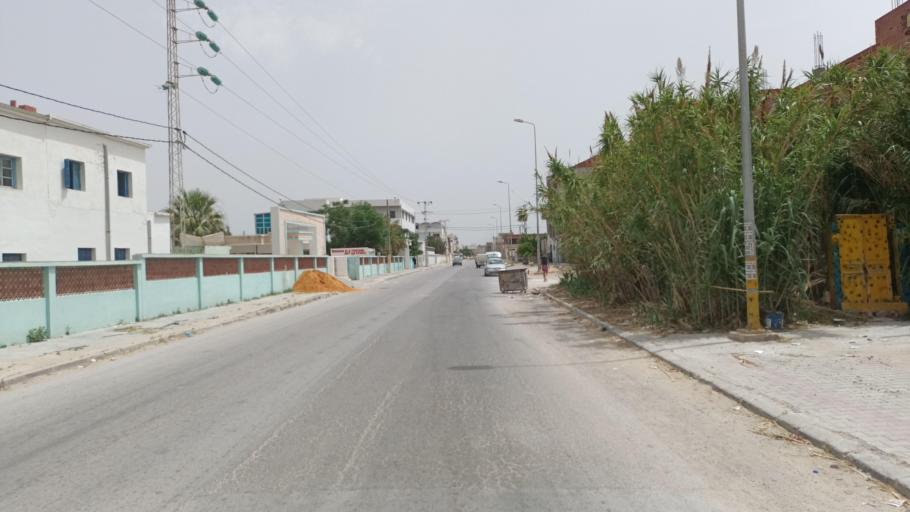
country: TN
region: Nabul
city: Manzil Bu Zalafah
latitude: 36.7077
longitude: 10.4846
